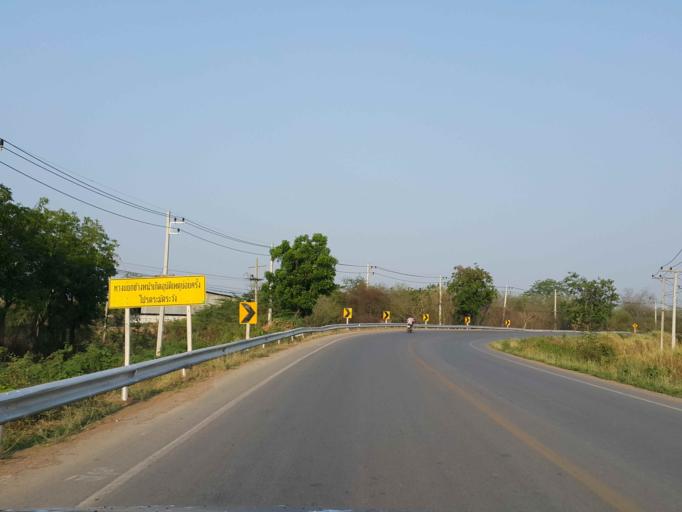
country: TH
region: Sukhothai
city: Sawankhalok
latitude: 17.3100
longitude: 99.8130
